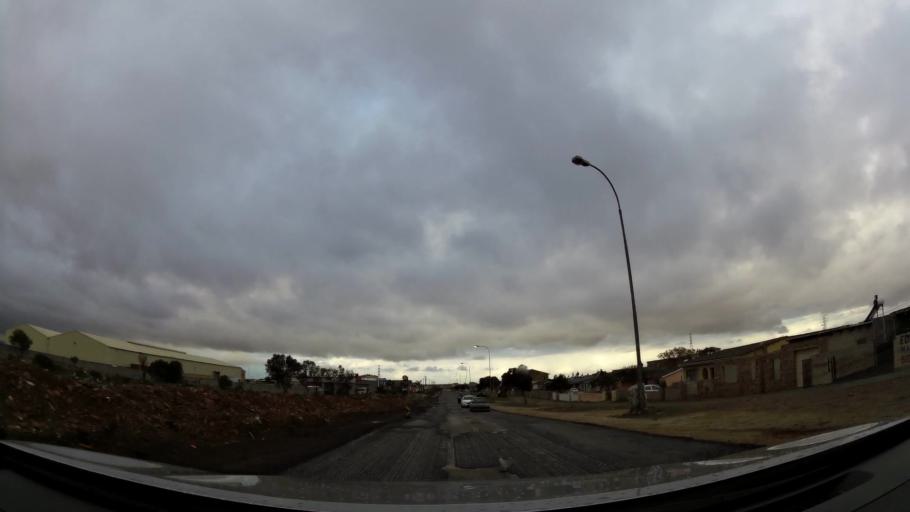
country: ZA
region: Eastern Cape
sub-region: Nelson Mandela Bay Metropolitan Municipality
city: Port Elizabeth
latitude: -33.8952
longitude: 25.5447
